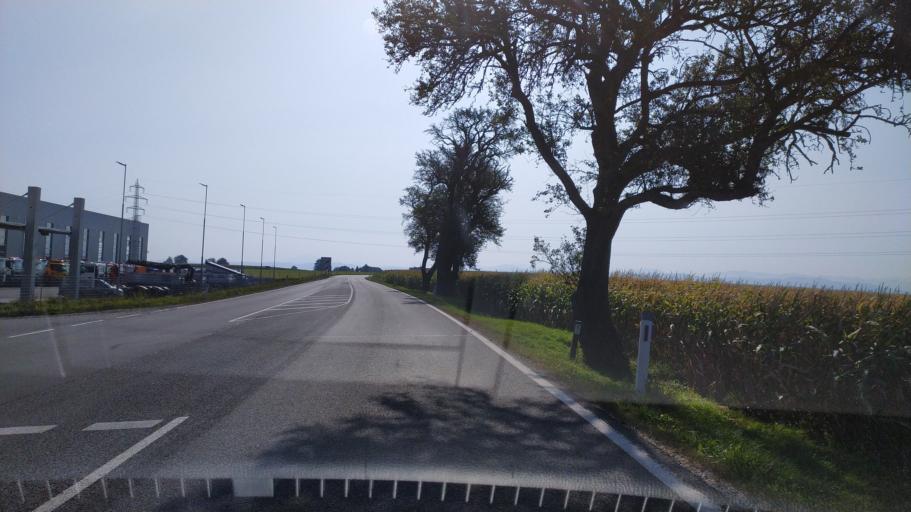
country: AT
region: Lower Austria
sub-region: Politischer Bezirk Amstetten
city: Zeillern
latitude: 48.1136
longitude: 14.7259
